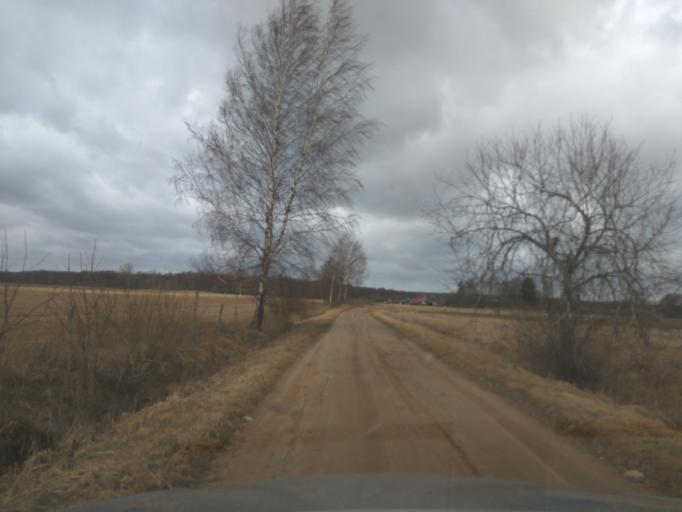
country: LV
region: Skrunda
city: Skrunda
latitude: 56.8366
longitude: 22.2152
